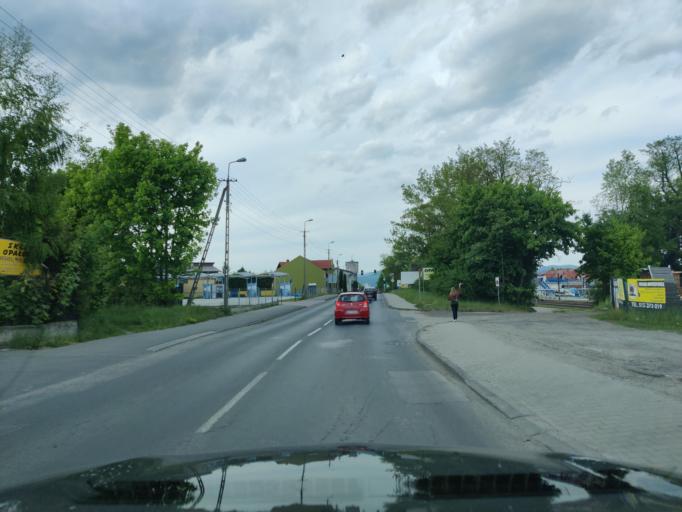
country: PL
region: Silesian Voivodeship
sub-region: Powiat zywiecki
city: Zywiec
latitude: 49.6773
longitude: 19.1833
